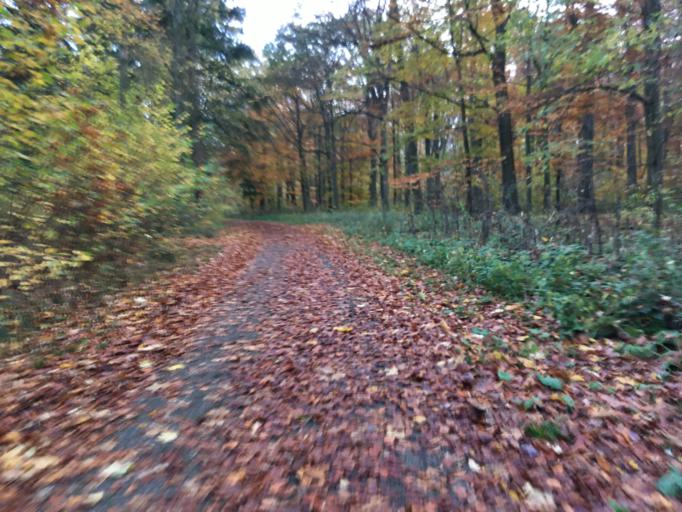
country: DE
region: Baden-Wuerttemberg
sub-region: Regierungsbezirk Stuttgart
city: Weinsberg
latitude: 49.1422
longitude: 9.2686
